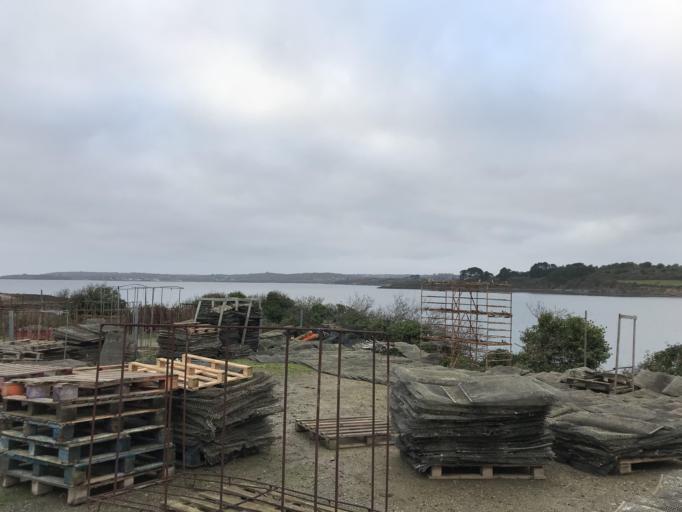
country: FR
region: Brittany
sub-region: Departement du Finistere
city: Logonna-Daoulas
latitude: 48.3351
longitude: -4.3168
